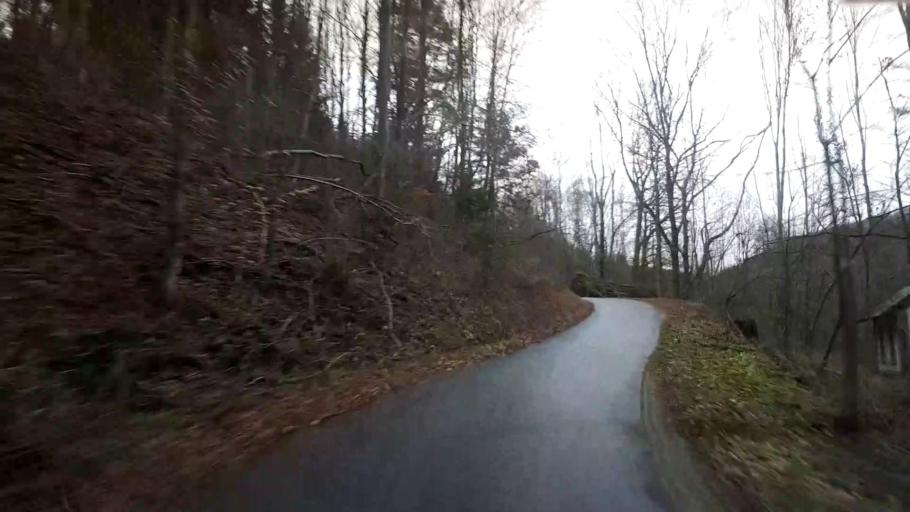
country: DE
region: Bavaria
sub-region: Upper Franconia
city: Wattendorf
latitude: 49.9984
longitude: 11.0916
